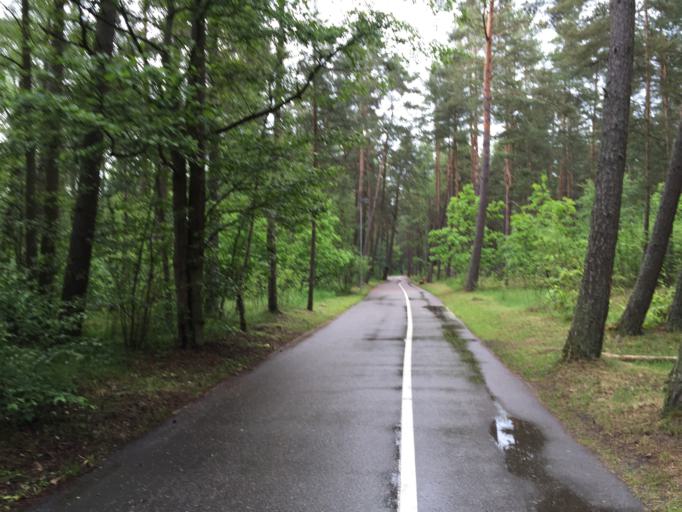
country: LT
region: Klaipedos apskritis
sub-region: Klaipeda
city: Klaipeda
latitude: 55.7506
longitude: 21.1182
